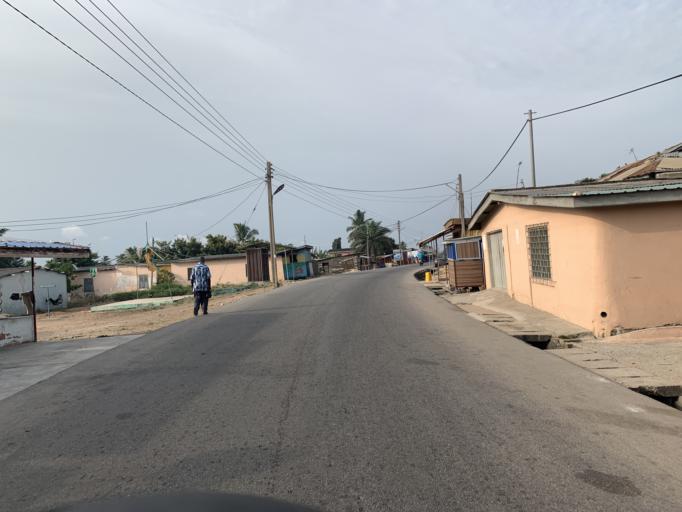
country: GH
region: Central
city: Winneba
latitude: 5.3488
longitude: -0.6286
